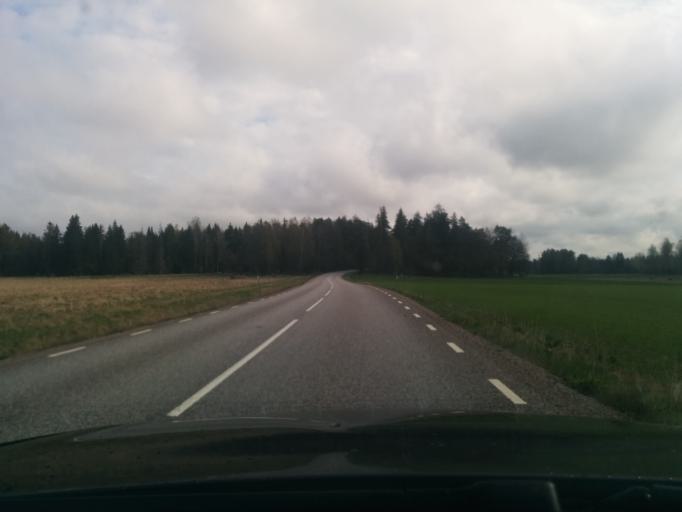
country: SE
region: Uppsala
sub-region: Tierps Kommun
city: Orbyhus
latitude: 60.1893
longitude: 17.6787
